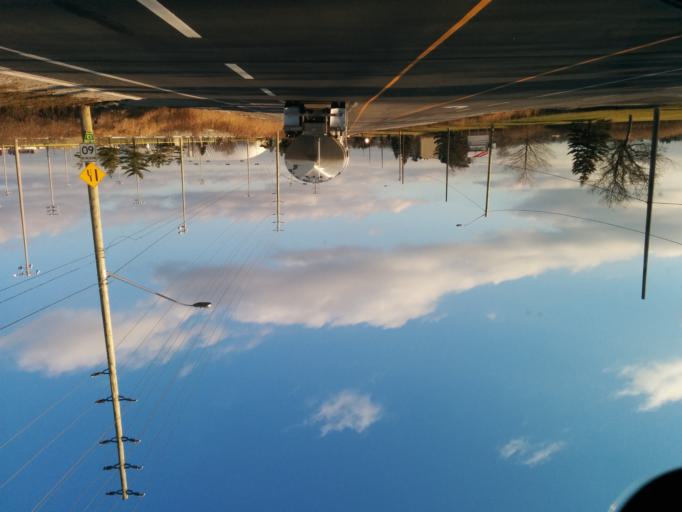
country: CA
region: Ontario
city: Oakville
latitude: 43.5090
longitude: -79.6983
